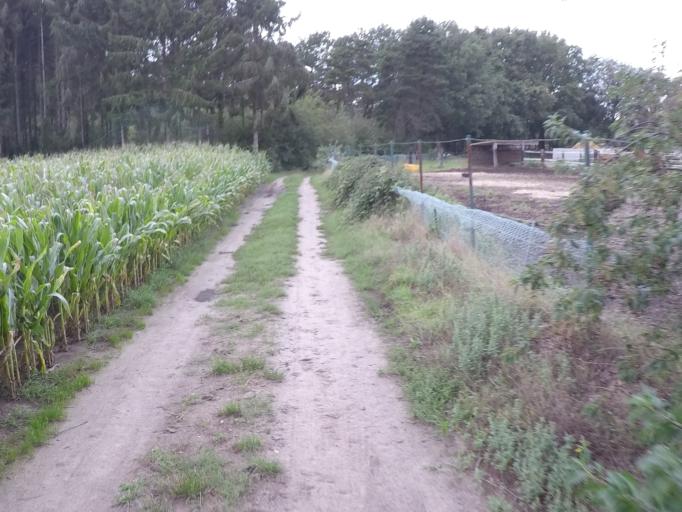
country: BE
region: Flanders
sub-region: Provincie Antwerpen
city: Grobbendonk
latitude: 51.2053
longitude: 4.7252
